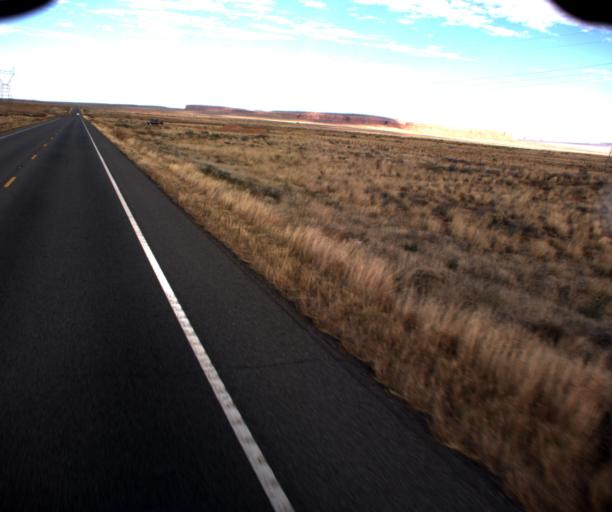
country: US
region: Arizona
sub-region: Apache County
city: Lukachukai
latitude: 36.9356
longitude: -109.2353
